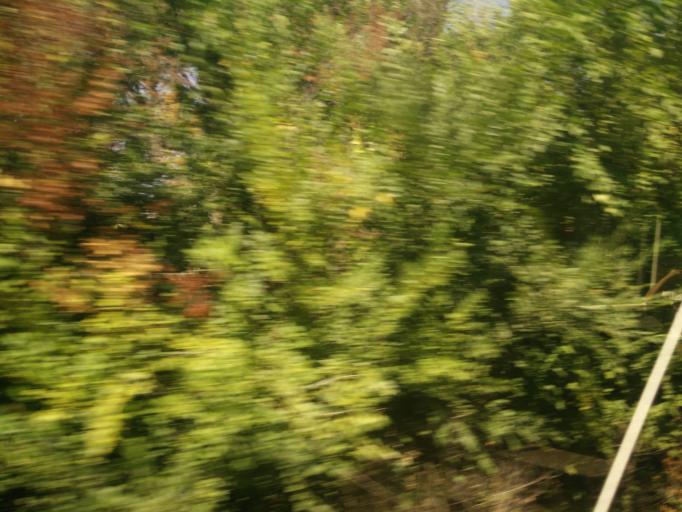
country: ES
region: Catalonia
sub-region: Provincia de Barcelona
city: Sant Adria de Besos
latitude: 41.4217
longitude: 2.2199
